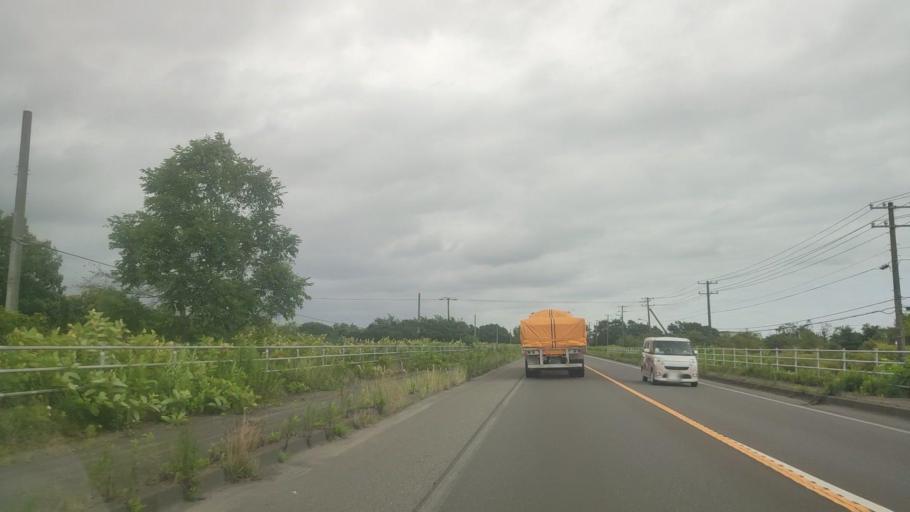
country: JP
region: Hokkaido
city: Shiraoi
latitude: 42.5208
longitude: 141.3082
